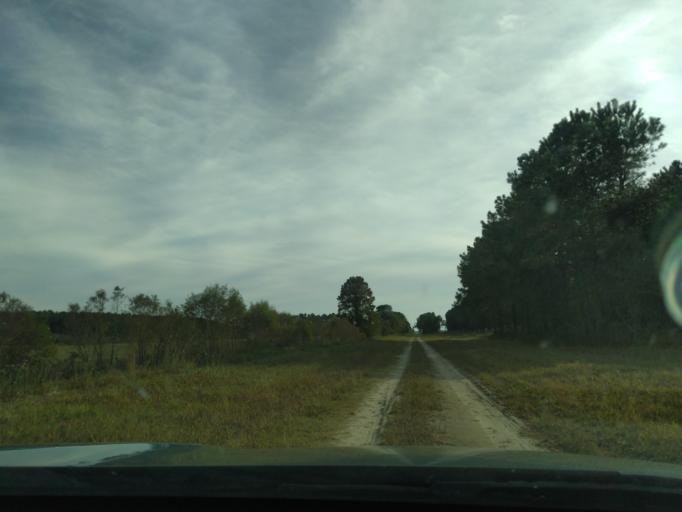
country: US
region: North Carolina
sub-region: Beaufort County
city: Belhaven
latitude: 35.6672
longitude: -76.5485
